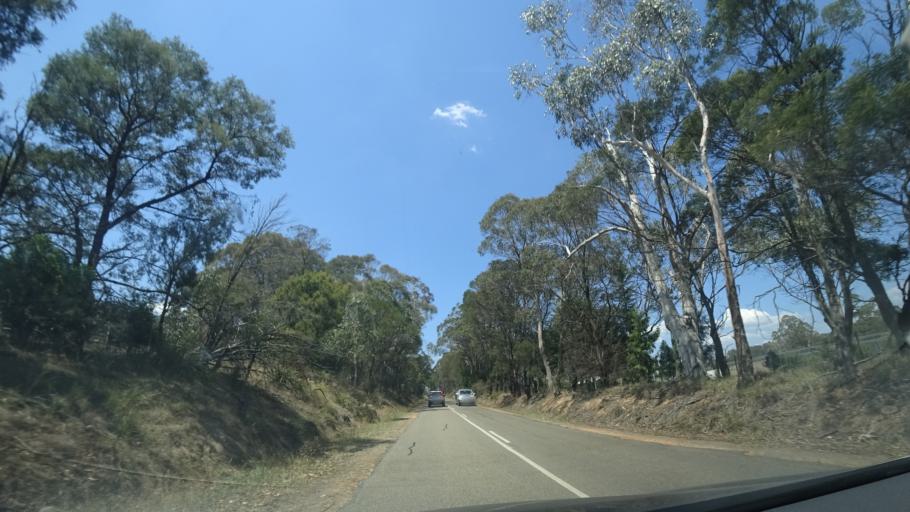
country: AU
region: New South Wales
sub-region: Wingecarribee
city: Bundanoon
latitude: -34.6110
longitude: 150.2418
